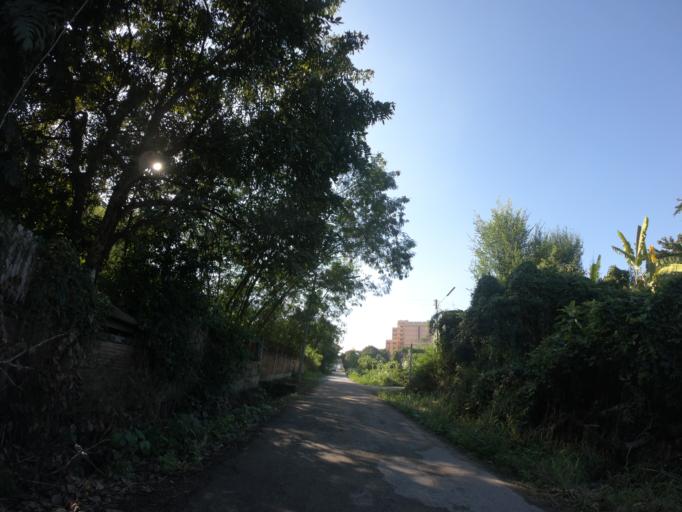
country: TH
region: Chiang Mai
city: Chiang Mai
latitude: 18.7862
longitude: 99.0239
